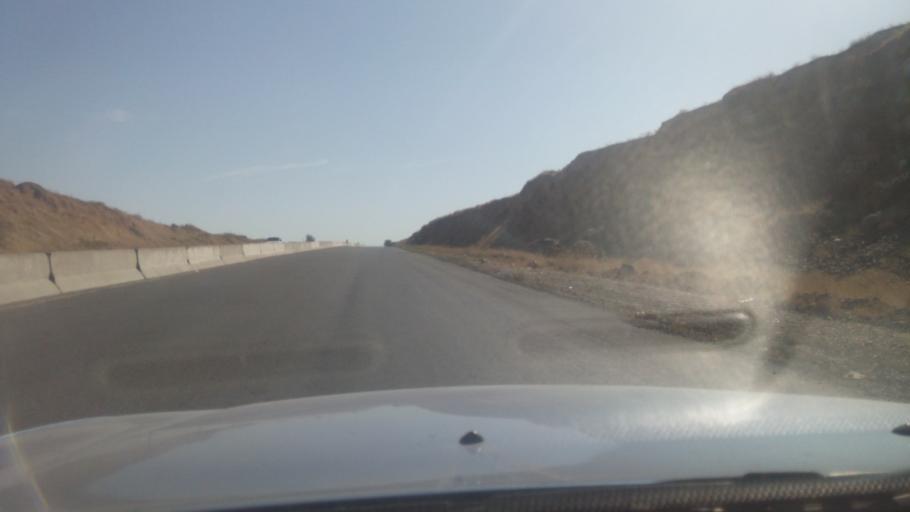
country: UZ
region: Jizzax
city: Jizzax
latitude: 40.0413
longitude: 67.6562
